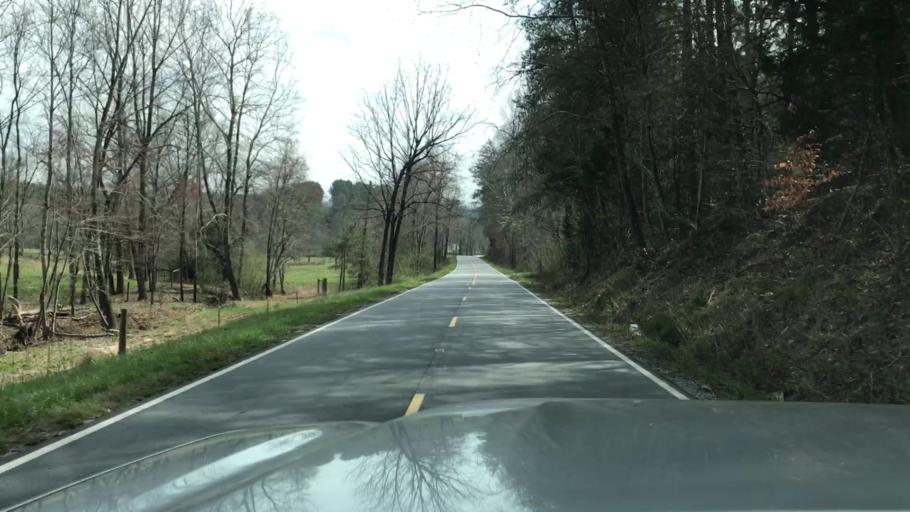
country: US
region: North Carolina
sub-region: Rutherford County
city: Spindale
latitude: 35.4511
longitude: -81.8821
